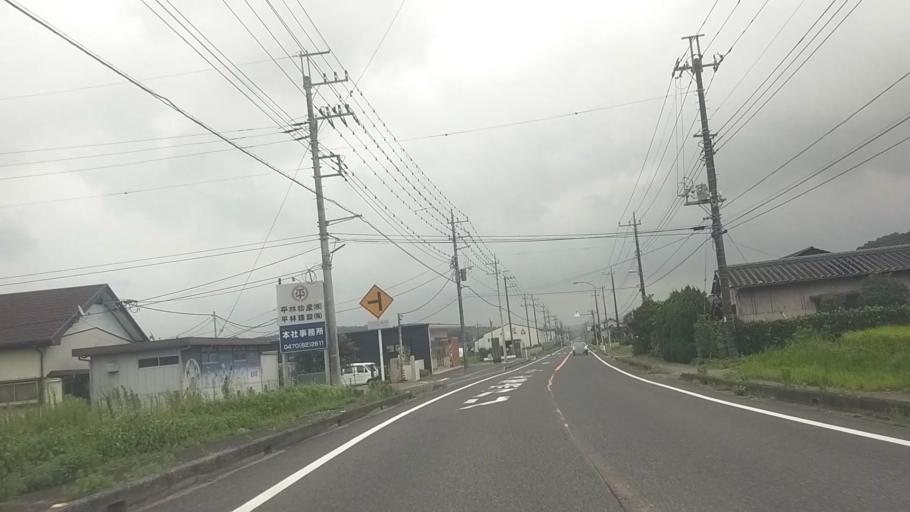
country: JP
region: Chiba
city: Ohara
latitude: 35.2878
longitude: 140.2574
